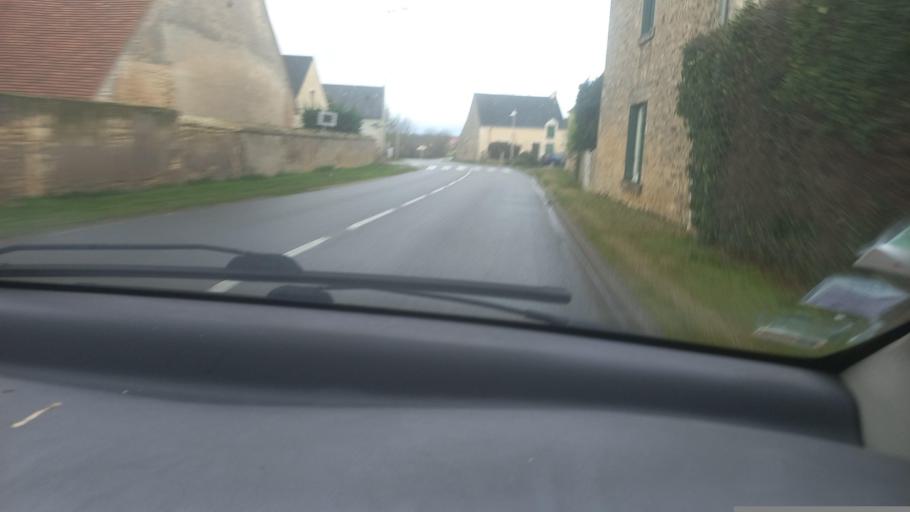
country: FR
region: Centre
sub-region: Departement de l'Indre
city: Neuvy-Pailloux
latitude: 46.7943
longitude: 1.9847
